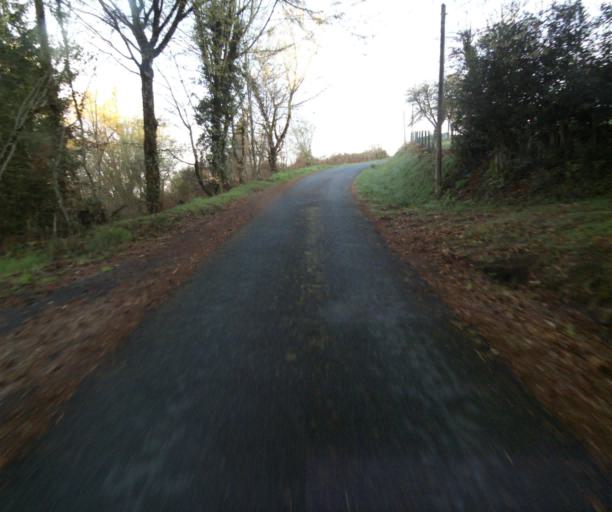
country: FR
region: Limousin
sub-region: Departement de la Correze
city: Naves
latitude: 45.3201
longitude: 1.8335
